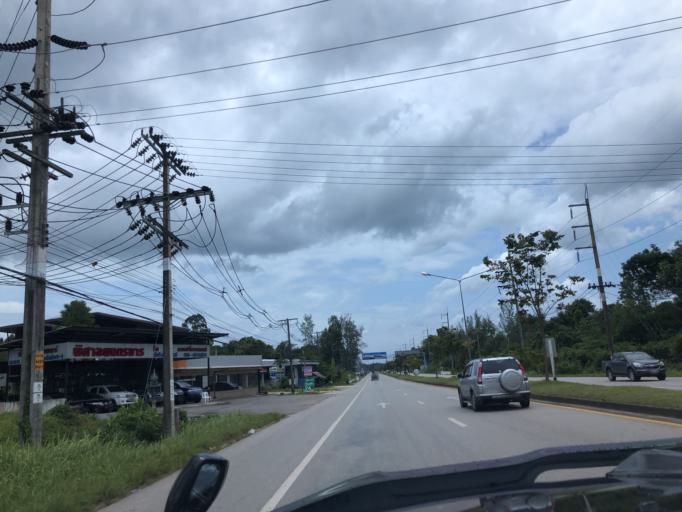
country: TH
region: Krabi
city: Khlong Thom
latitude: 7.9693
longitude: 99.1407
